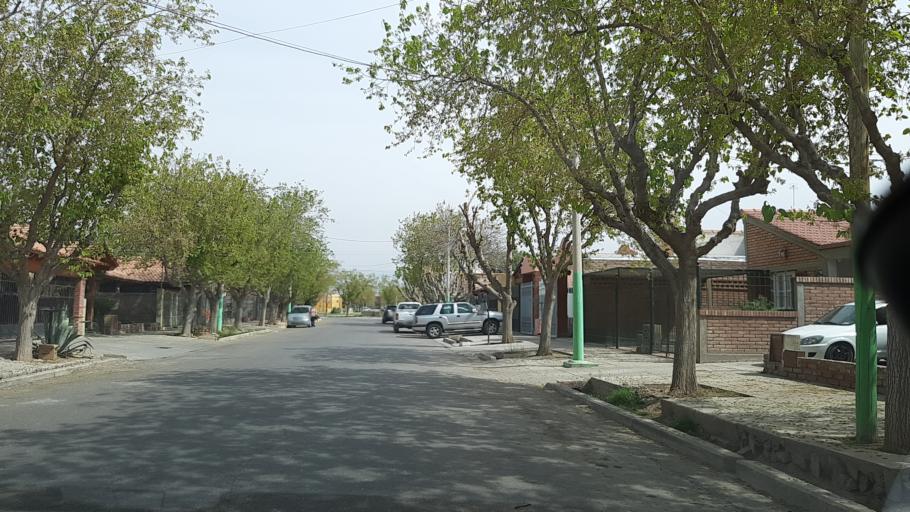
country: AR
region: San Juan
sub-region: Departamento de Rivadavia
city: Rivadavia
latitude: -31.5348
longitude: -68.5984
